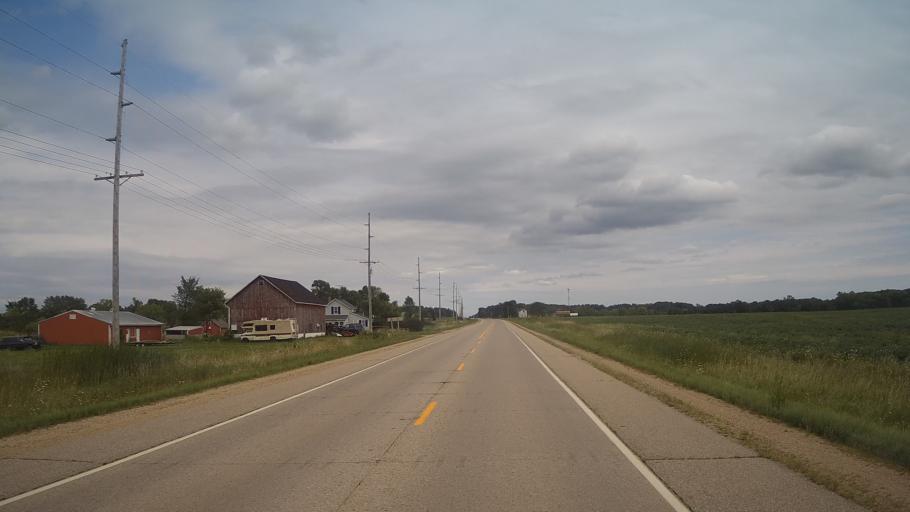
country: US
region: Wisconsin
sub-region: Waushara County
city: Redgranite
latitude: 44.0411
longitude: -89.0159
